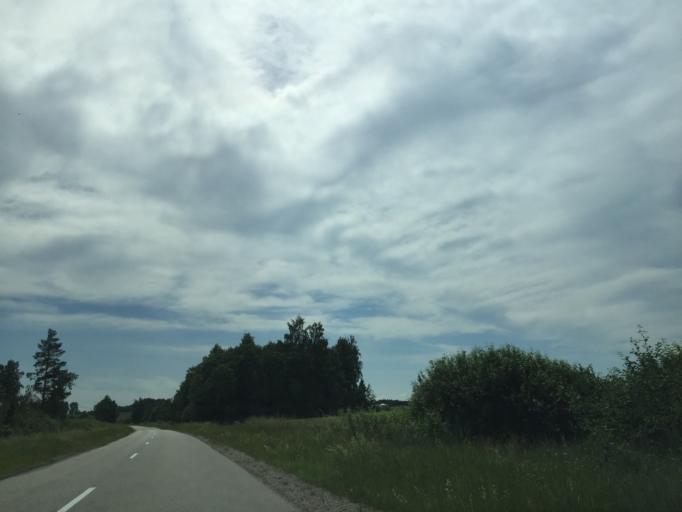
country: LV
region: Engure
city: Smarde
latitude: 57.0410
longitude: 23.2570
